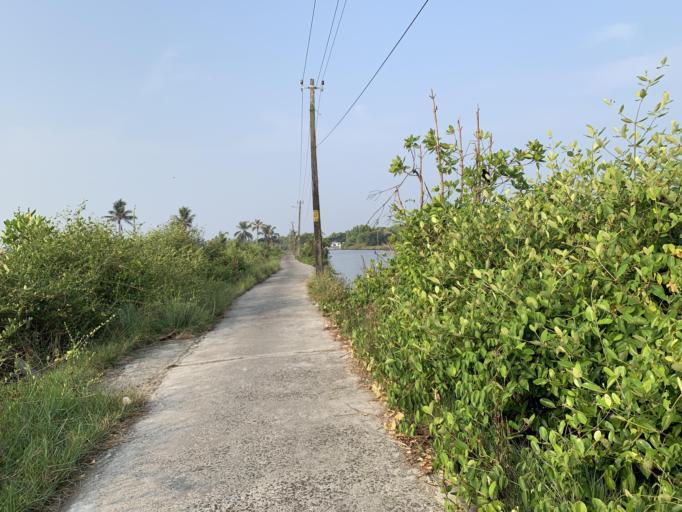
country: IN
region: Kerala
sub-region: Ernakulam
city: Elur
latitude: 10.0192
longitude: 76.2225
